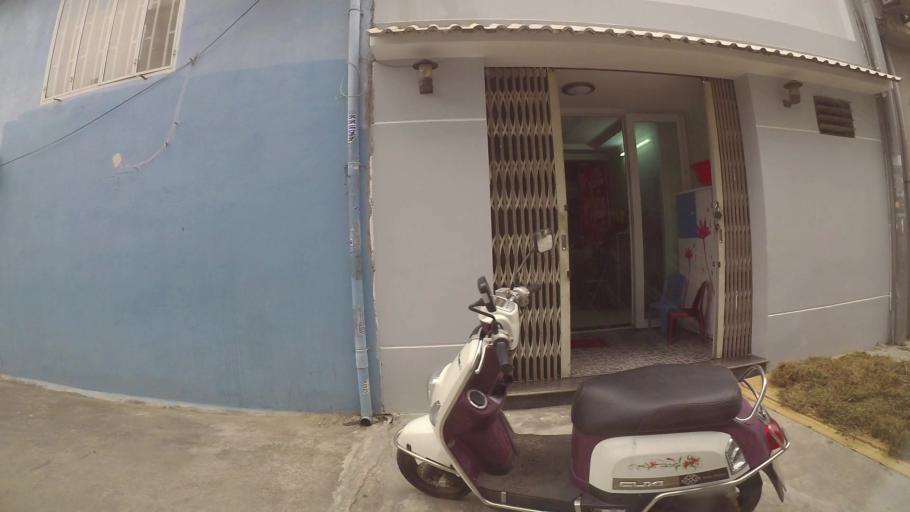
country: VN
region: Da Nang
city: Thanh Khe
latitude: 16.0569
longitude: 108.1838
